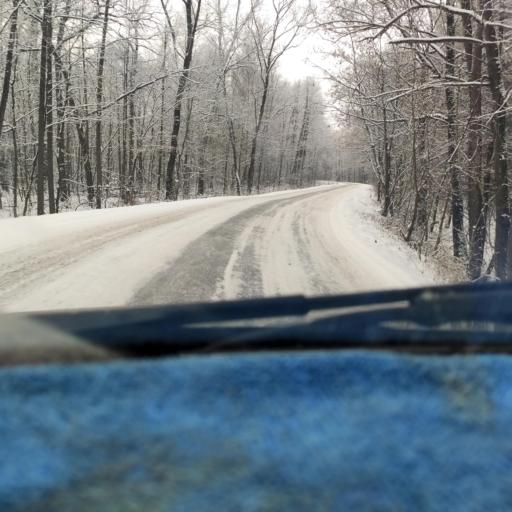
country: RU
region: Bashkortostan
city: Avdon
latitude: 54.6734
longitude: 55.8426
